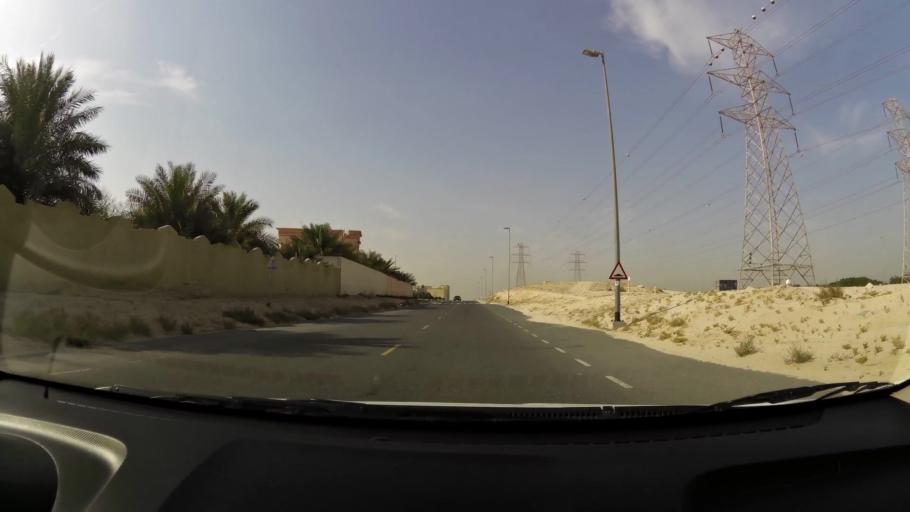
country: AE
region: Ash Shariqah
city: Sharjah
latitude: 25.2430
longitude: 55.4067
